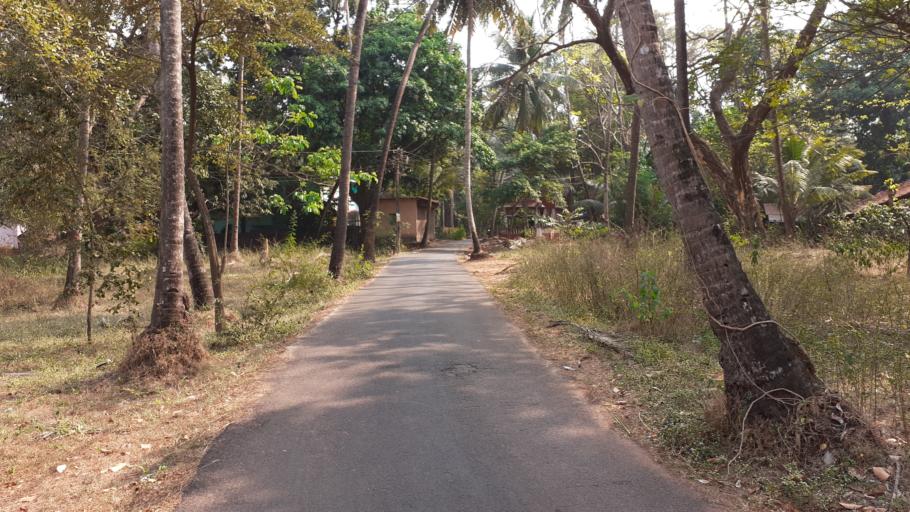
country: IN
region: Goa
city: Calangute
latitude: 15.5669
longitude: 73.7623
